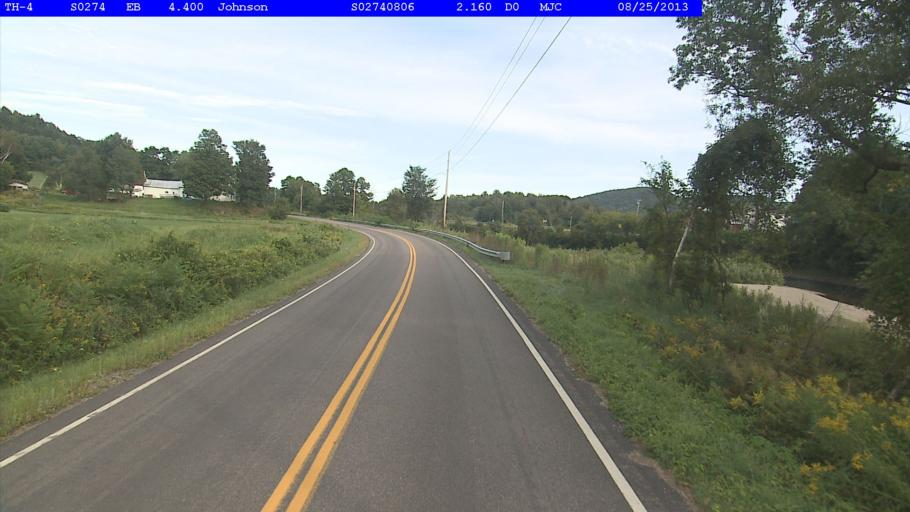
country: US
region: Vermont
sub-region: Lamoille County
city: Johnson
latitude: 44.6438
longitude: -72.7141
